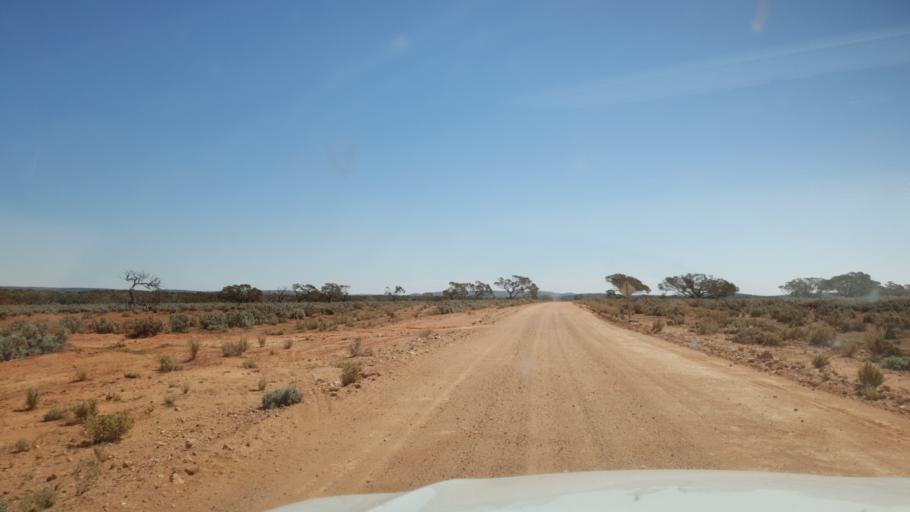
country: AU
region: South Australia
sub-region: Whyalla
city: Whyalla
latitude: -32.6313
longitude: 136.8385
